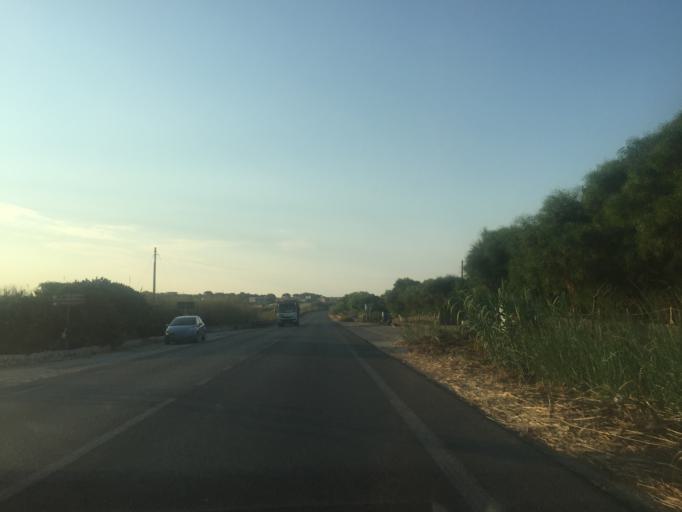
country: IT
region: Sicily
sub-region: Ragusa
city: Cava d'Aliga
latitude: 36.7197
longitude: 14.7541
